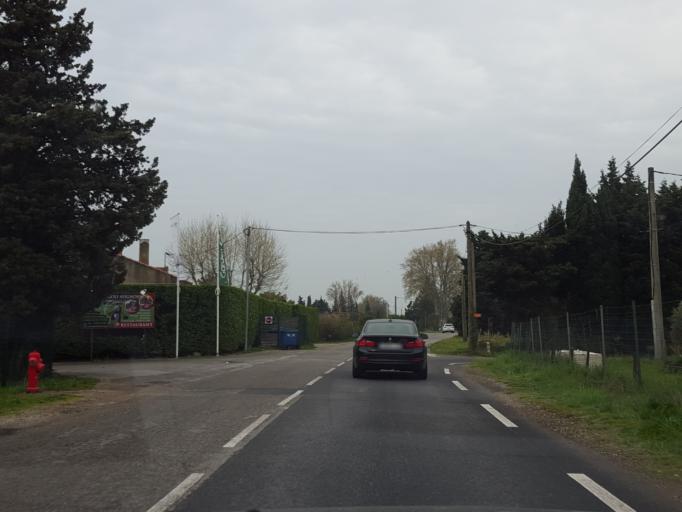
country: FR
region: Provence-Alpes-Cote d'Azur
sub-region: Departement du Vaucluse
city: Morieres-les-Avignon
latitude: 43.9243
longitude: 4.9012
